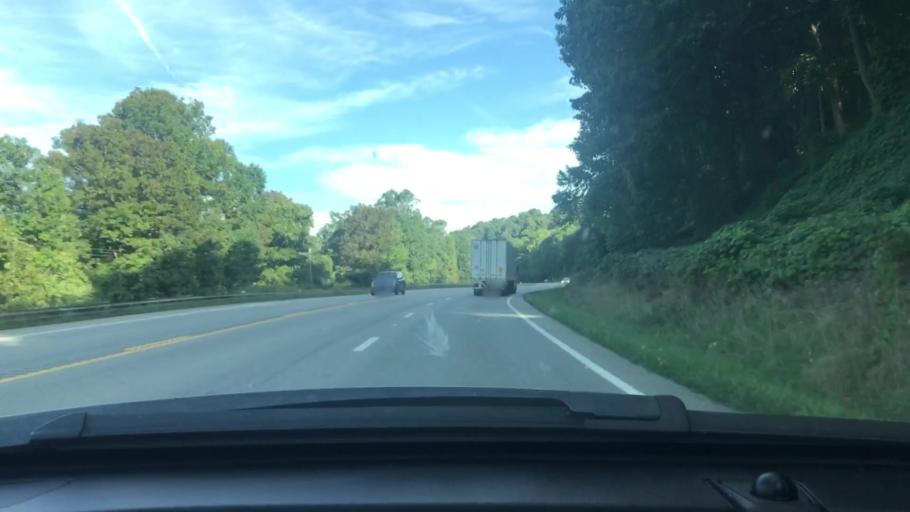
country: US
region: Arkansas
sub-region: Sharp County
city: Cherokee Village
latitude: 36.3025
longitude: -91.4133
